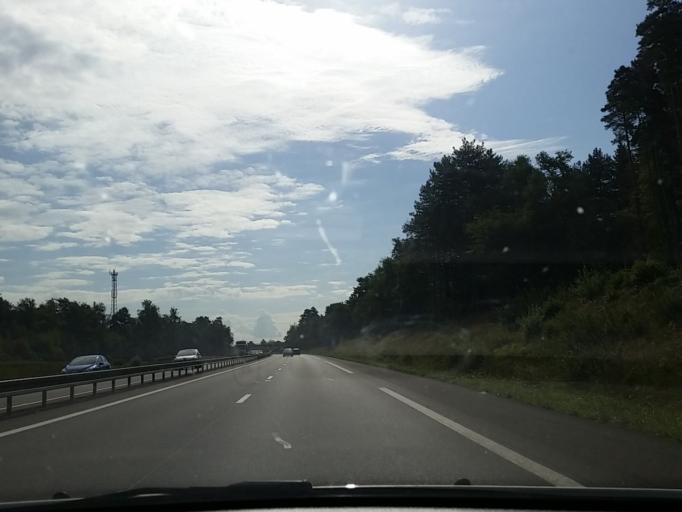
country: FR
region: Centre
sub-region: Departement du Loir-et-Cher
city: Chatres-sur-Cher
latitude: 47.2904
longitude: 1.9643
